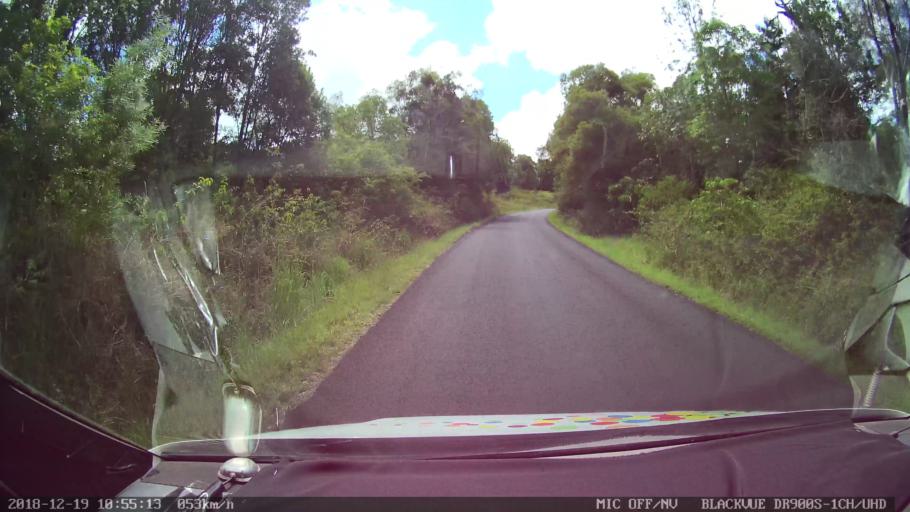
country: AU
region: New South Wales
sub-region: Lismore Municipality
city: Nimbin
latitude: -28.5937
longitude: 153.2527
